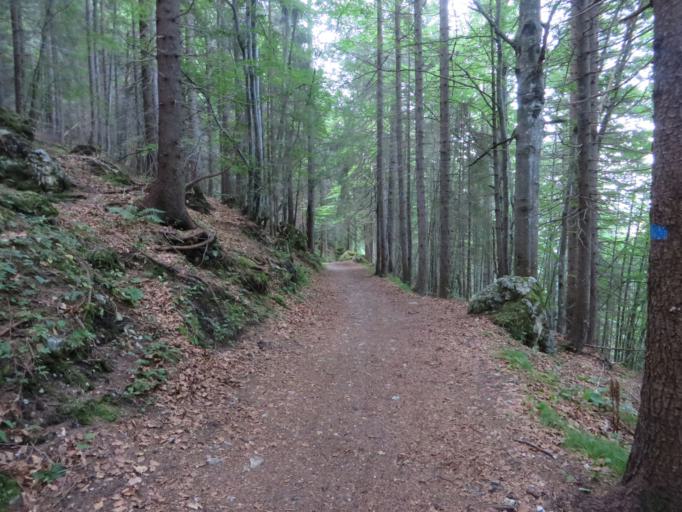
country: IT
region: Trentino-Alto Adige
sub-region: Provincia di Trento
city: Carisolo
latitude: 46.2159
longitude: 10.8269
